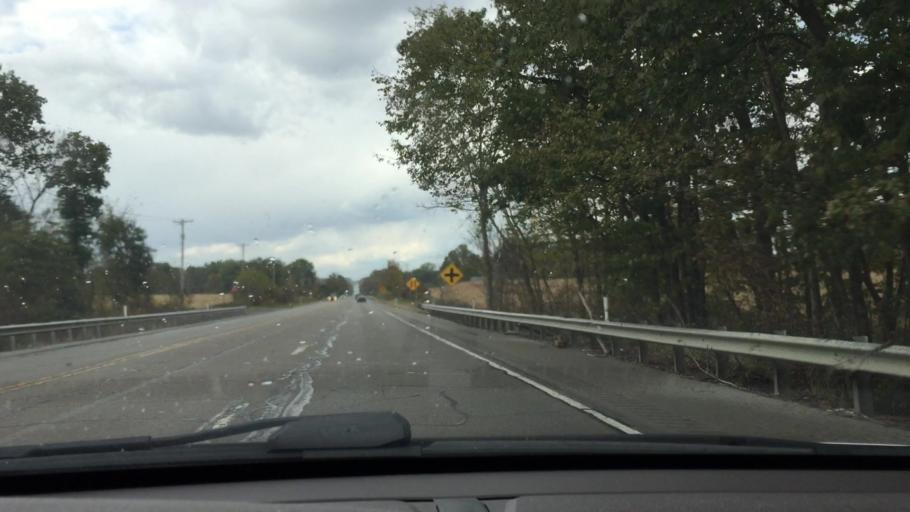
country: US
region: Ohio
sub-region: Mahoning County
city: Lowellville
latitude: 41.0659
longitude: -80.4628
